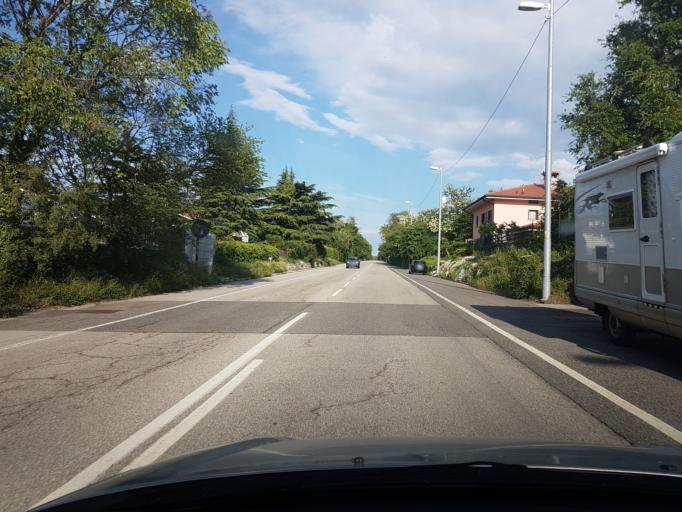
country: IT
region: Friuli Venezia Giulia
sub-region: Provincia di Trieste
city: Villa Opicina
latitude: 45.6823
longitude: 13.7875
